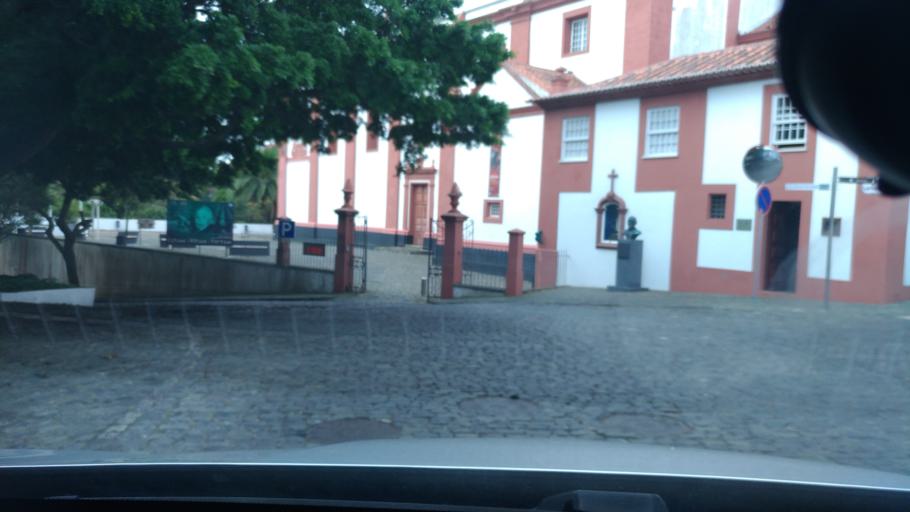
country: PT
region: Azores
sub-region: Angra do Heroismo
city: Angra do Heroismo
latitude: 38.6567
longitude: -27.2163
